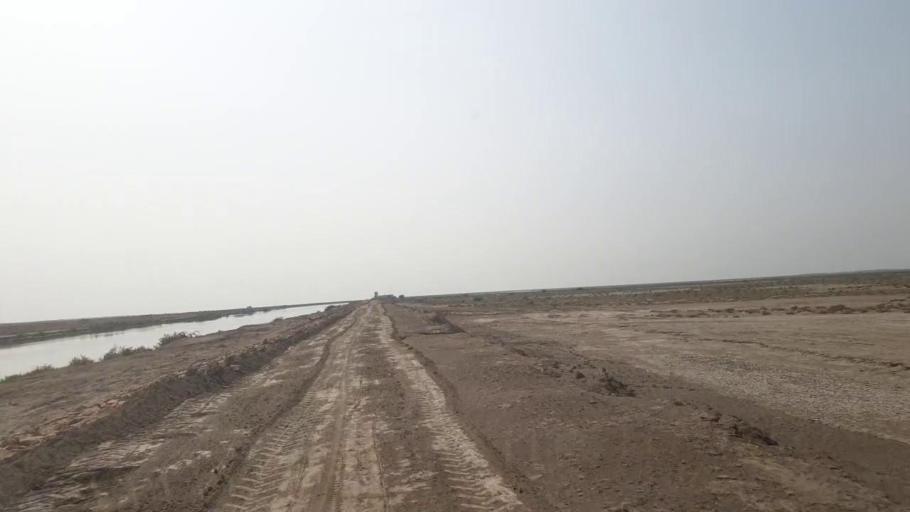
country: PK
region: Sindh
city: Kadhan
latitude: 24.3286
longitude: 68.8309
